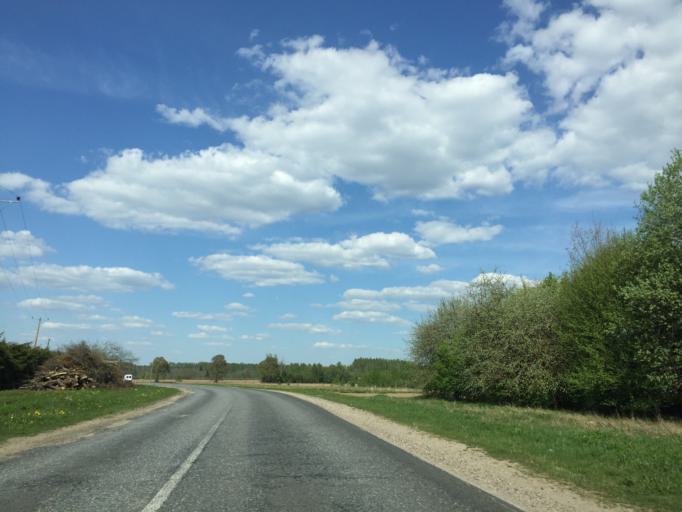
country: LV
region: Limbazu Rajons
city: Limbazi
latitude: 57.4307
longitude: 24.7136
